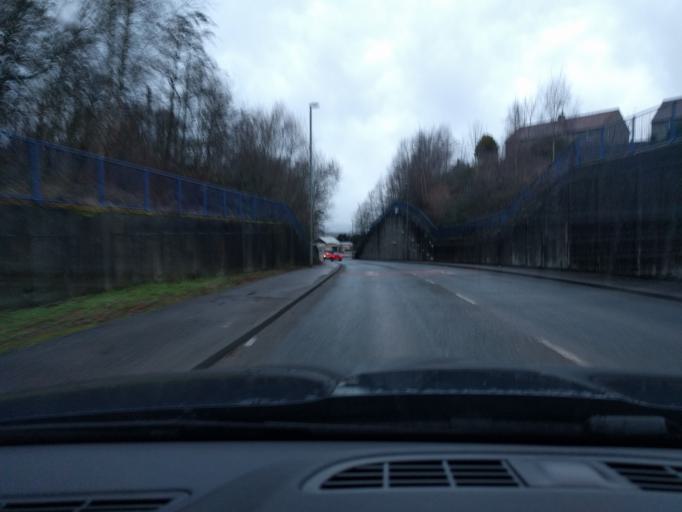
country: GB
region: Scotland
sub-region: Falkirk
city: Falkirk
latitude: 55.9941
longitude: -3.7525
